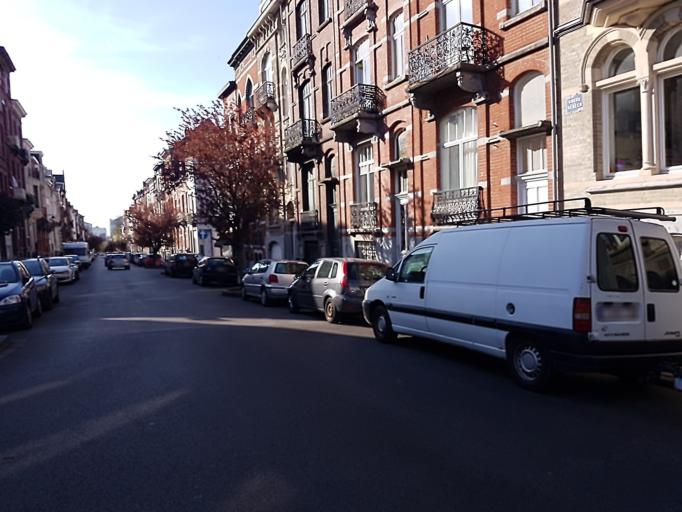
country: BE
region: Brussels Capital
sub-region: Bruxelles-Capitale
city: Brussels
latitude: 50.8473
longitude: 4.3908
